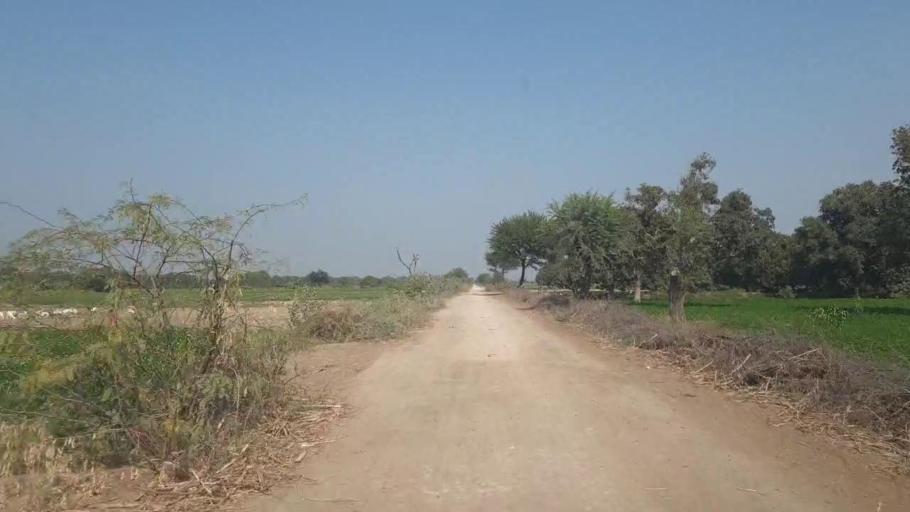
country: PK
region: Sindh
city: Tando Allahyar
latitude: 25.4400
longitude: 68.8499
